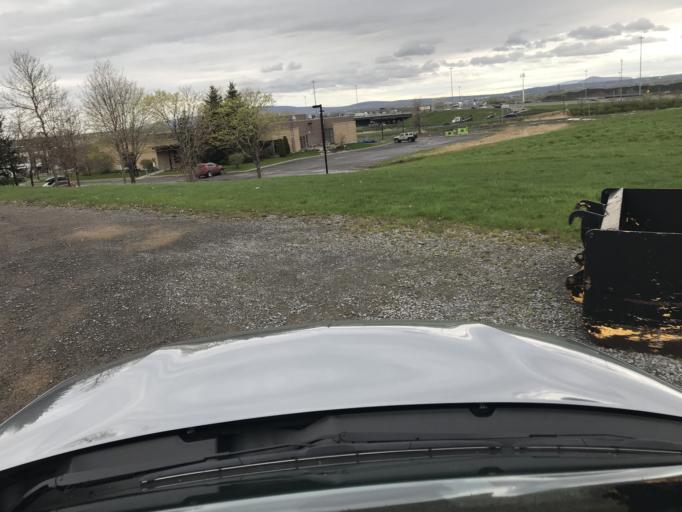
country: CA
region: Quebec
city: L'Ancienne-Lorette
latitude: 46.7922
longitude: -71.2826
